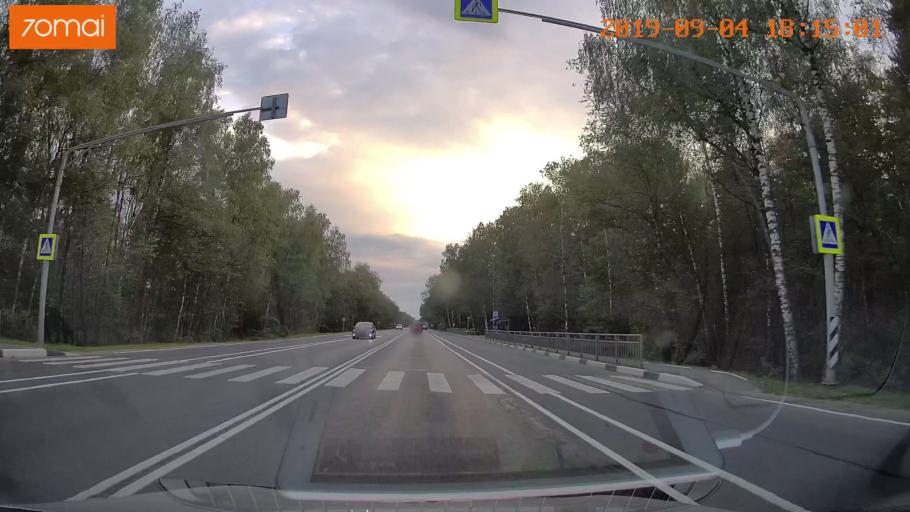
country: RU
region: Moskovskaya
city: Lopatinskiy
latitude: 55.3492
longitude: 38.7109
